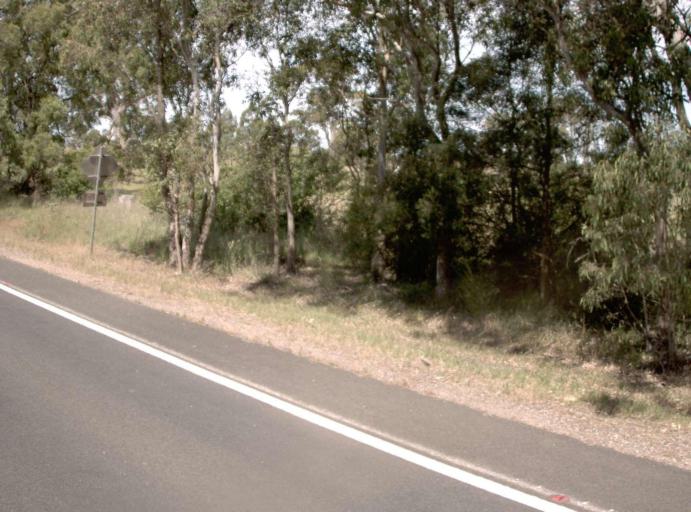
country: AU
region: Victoria
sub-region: Wellington
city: Sale
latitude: -37.9529
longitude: 147.1068
